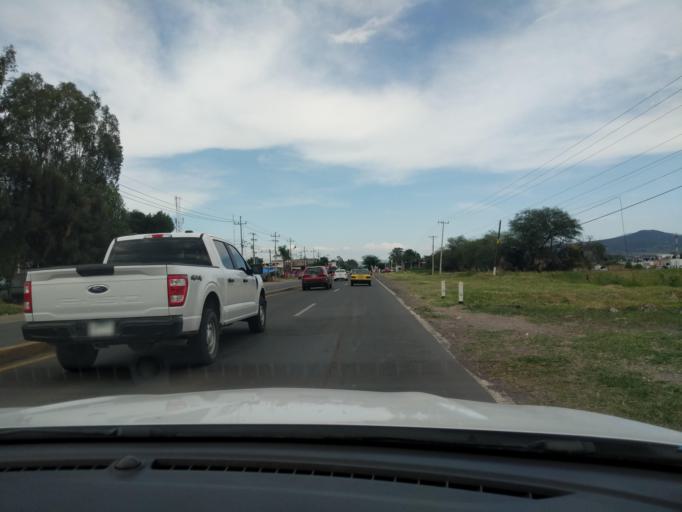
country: MX
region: Jalisco
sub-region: El Salto
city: Galaxia Bonito Jalisco
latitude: 20.5080
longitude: -103.2039
